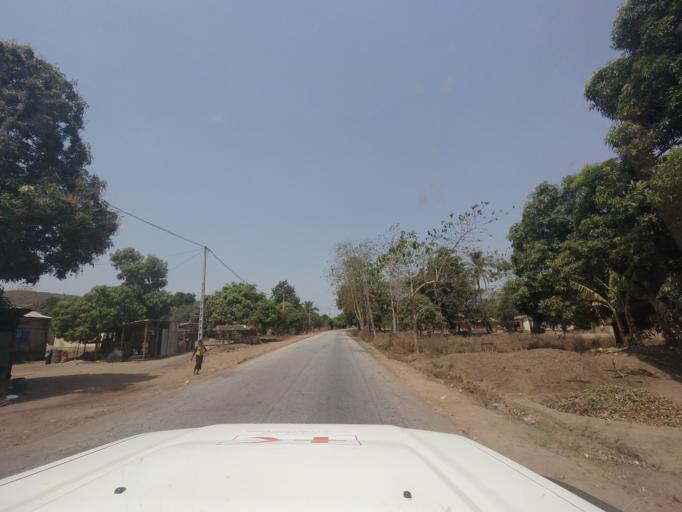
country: GN
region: Kindia
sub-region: Kindia
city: Kindia
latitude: 9.8654
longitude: -13.0616
